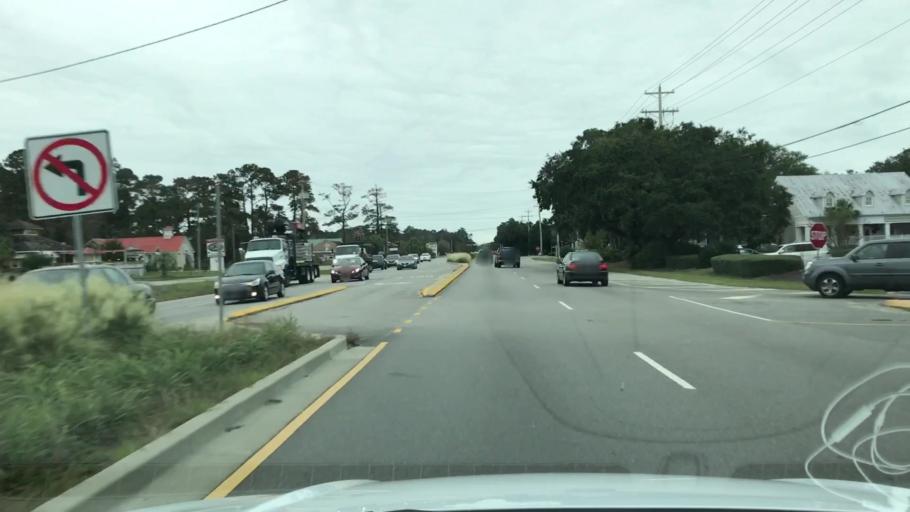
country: US
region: South Carolina
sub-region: Georgetown County
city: Murrells Inlet
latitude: 33.4460
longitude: -79.1220
